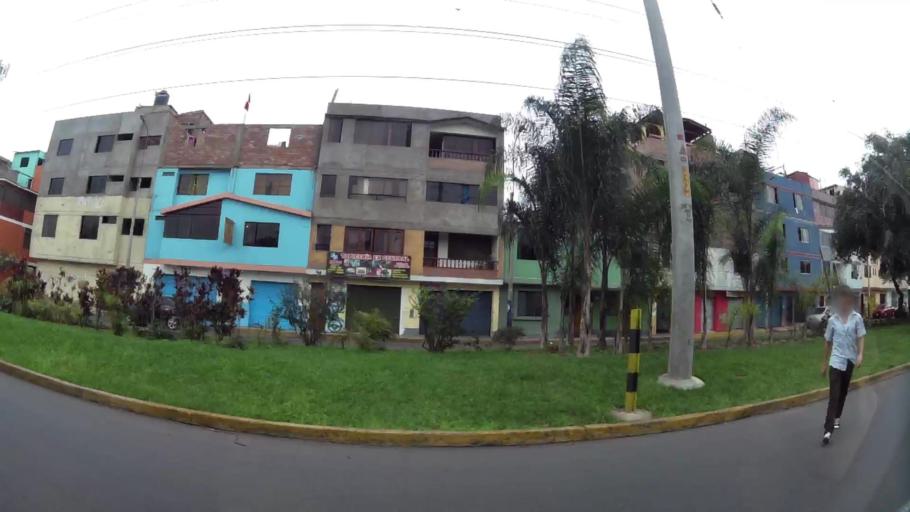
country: PE
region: Lima
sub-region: Lima
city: Surco
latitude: -12.1162
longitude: -76.9959
